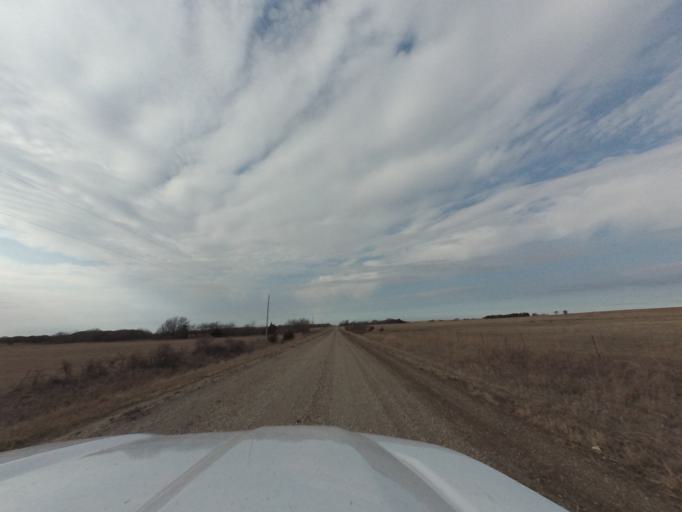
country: US
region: Kansas
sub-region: Chase County
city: Cottonwood Falls
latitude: 38.2170
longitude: -96.6870
